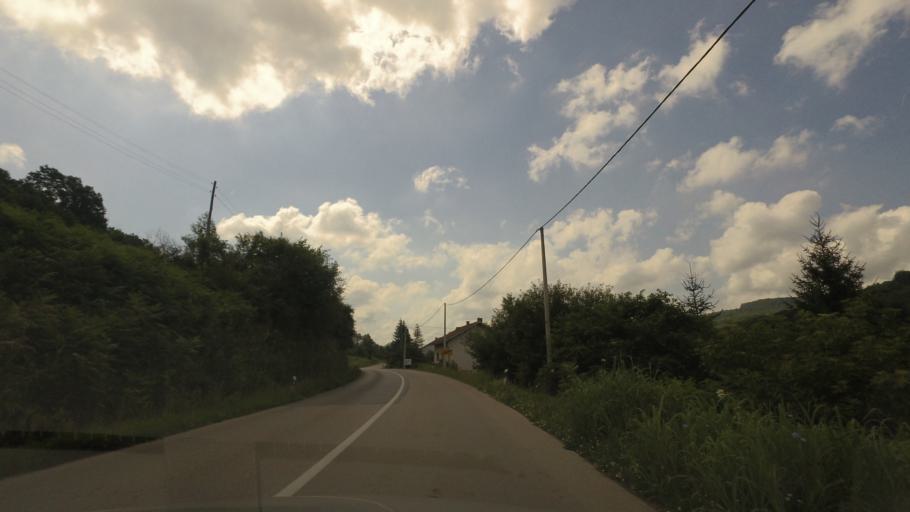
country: HR
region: Karlovacka
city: Vojnic
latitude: 45.3681
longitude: 15.6622
